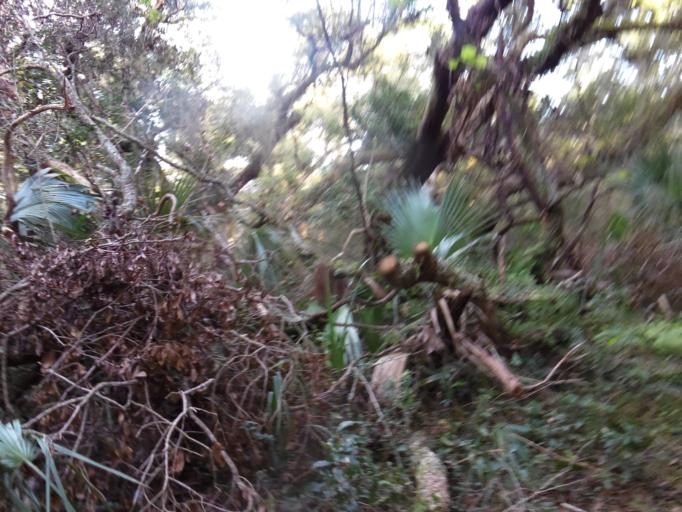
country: US
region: Florida
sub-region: Duval County
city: Atlantic Beach
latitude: 30.4712
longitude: -81.4190
